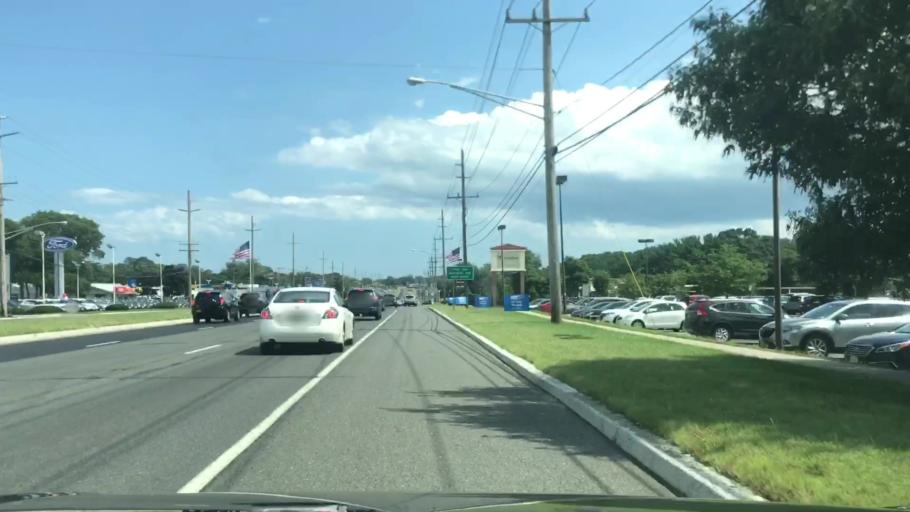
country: US
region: New Jersey
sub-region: Ocean County
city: Pine Beach
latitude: 39.9586
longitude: -74.1732
